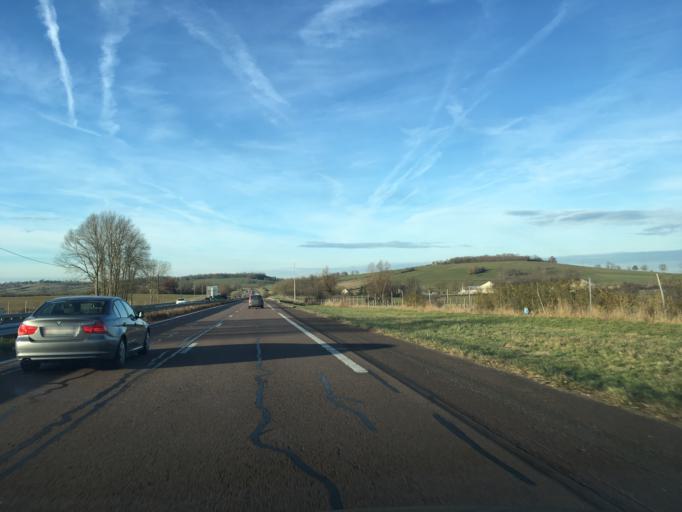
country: FR
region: Bourgogne
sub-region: Departement de l'Yonne
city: Avallon
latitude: 47.5353
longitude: 3.9788
